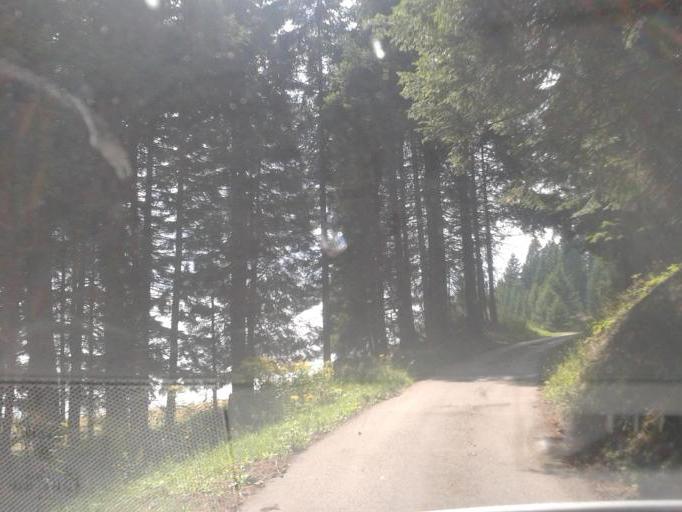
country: IT
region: Trentino-Alto Adige
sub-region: Provincia di Trento
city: Lodrone-Darzo
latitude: 45.8635
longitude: 10.5343
